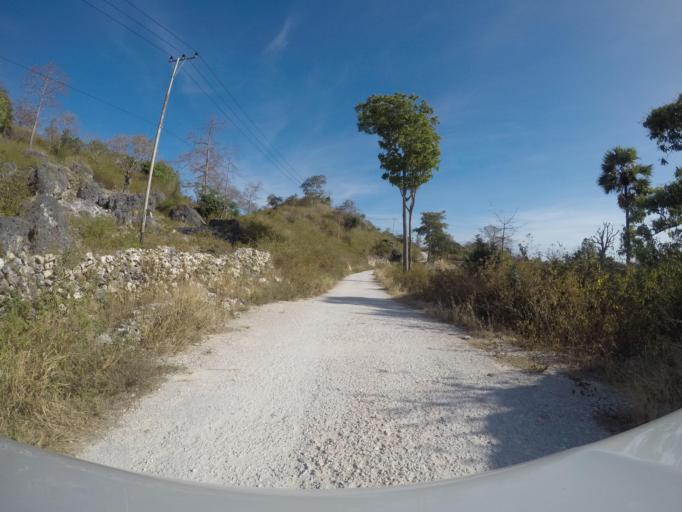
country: TL
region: Baucau
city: Baucau
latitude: -8.4482
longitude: 126.4269
